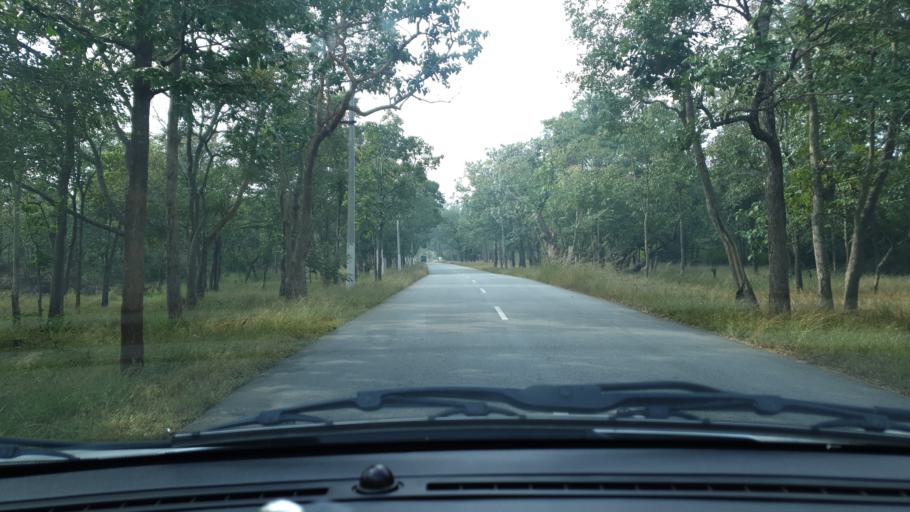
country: IN
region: Andhra Pradesh
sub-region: Kurnool
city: Srisailam
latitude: 16.2840
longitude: 78.7271
